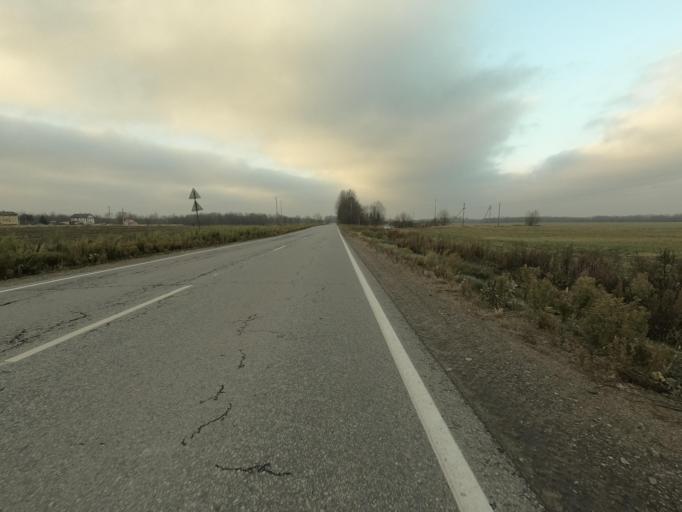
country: RU
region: Leningrad
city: Mga
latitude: 59.7654
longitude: 31.0188
